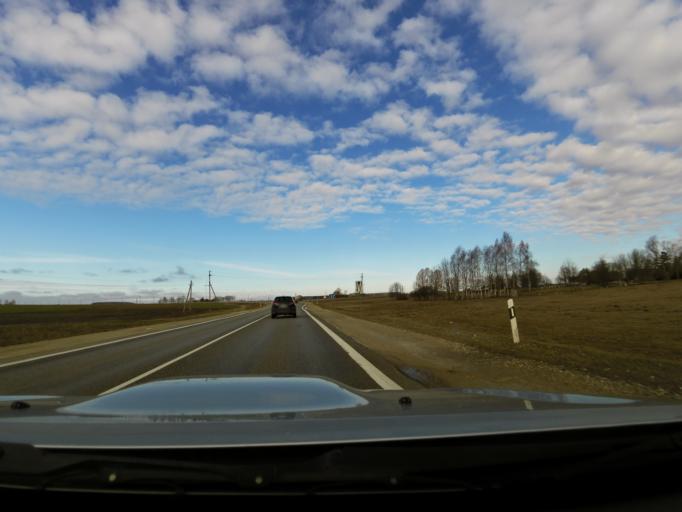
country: LT
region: Siauliu apskritis
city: Pakruojis
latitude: 55.7990
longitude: 24.0104
